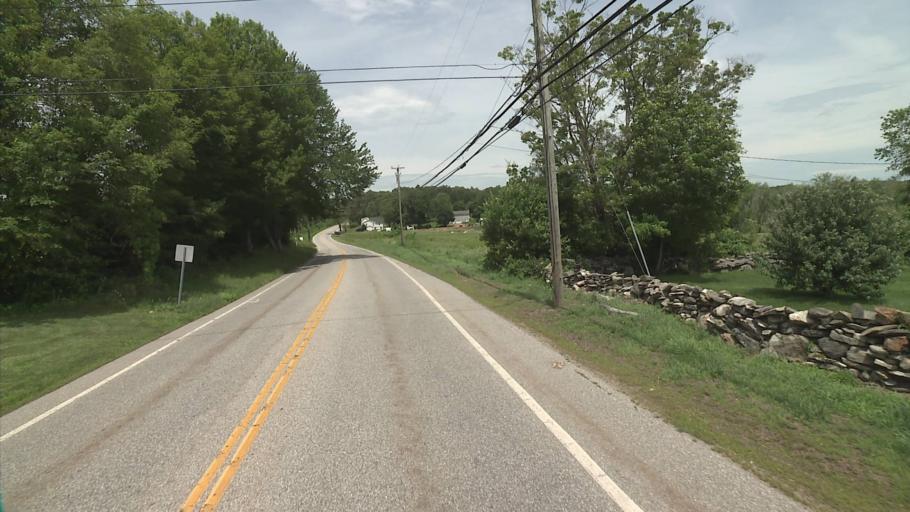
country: US
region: Connecticut
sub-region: New London County
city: Jewett City
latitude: 41.5804
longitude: -71.9774
